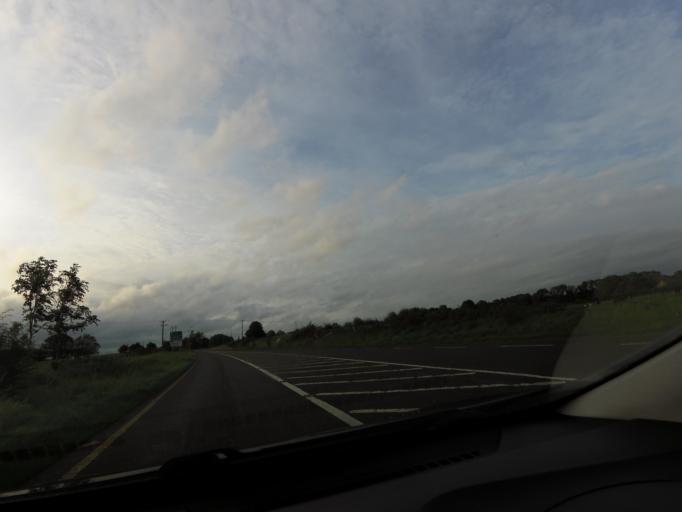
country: IE
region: Leinster
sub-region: Uibh Fhaili
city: Ferbane
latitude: 53.3022
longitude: -7.8190
